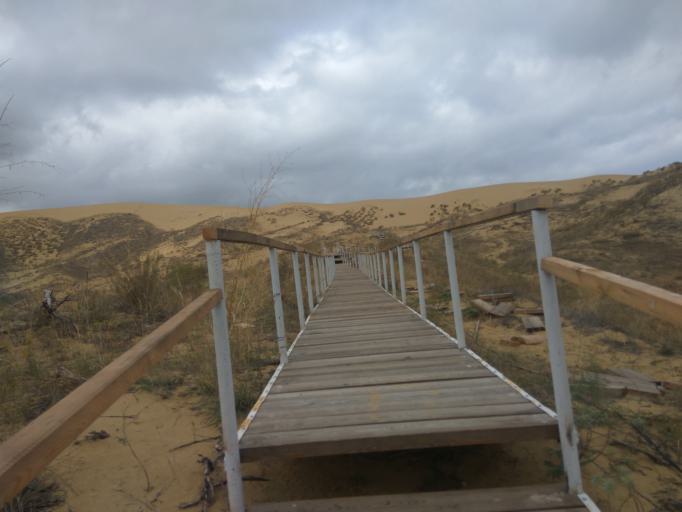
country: RU
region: Dagestan
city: Korkmaskala
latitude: 43.0052
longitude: 47.2359
